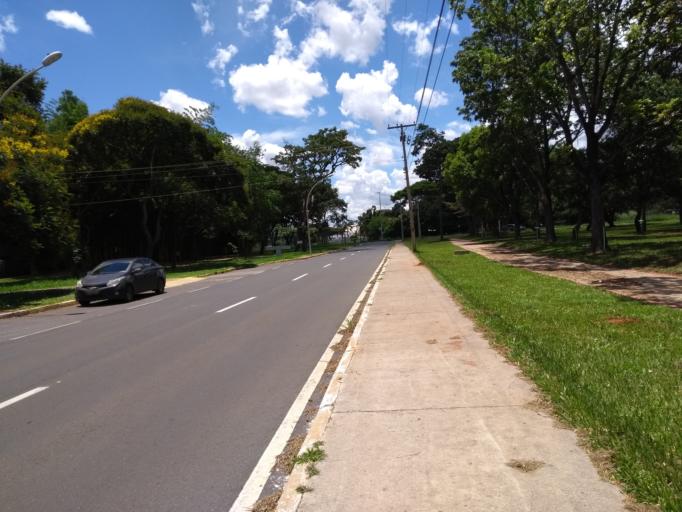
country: BR
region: Federal District
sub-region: Brasilia
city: Brasilia
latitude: -15.7721
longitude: -47.8712
